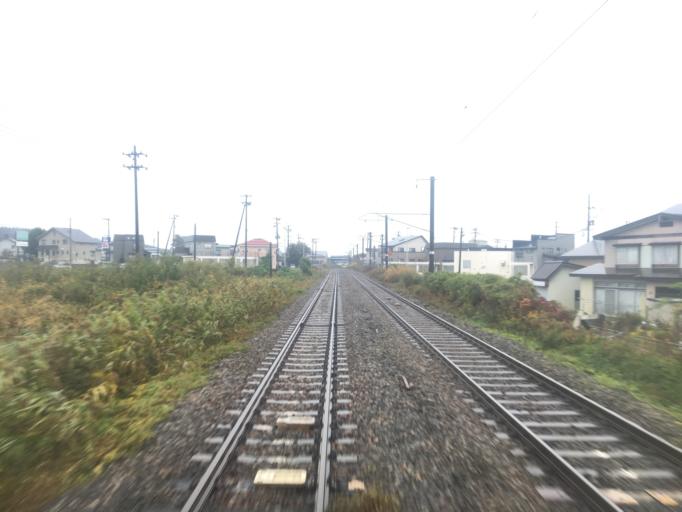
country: JP
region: Yamagata
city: Shinjo
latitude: 38.7507
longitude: 140.3077
